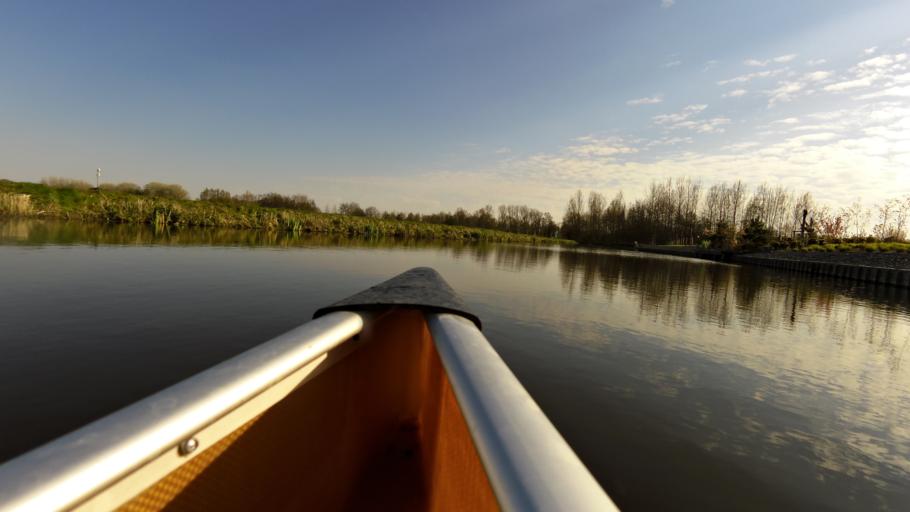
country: NL
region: South Holland
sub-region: Gemeente Teylingen
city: Sassenheim
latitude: 52.2253
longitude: 4.5382
